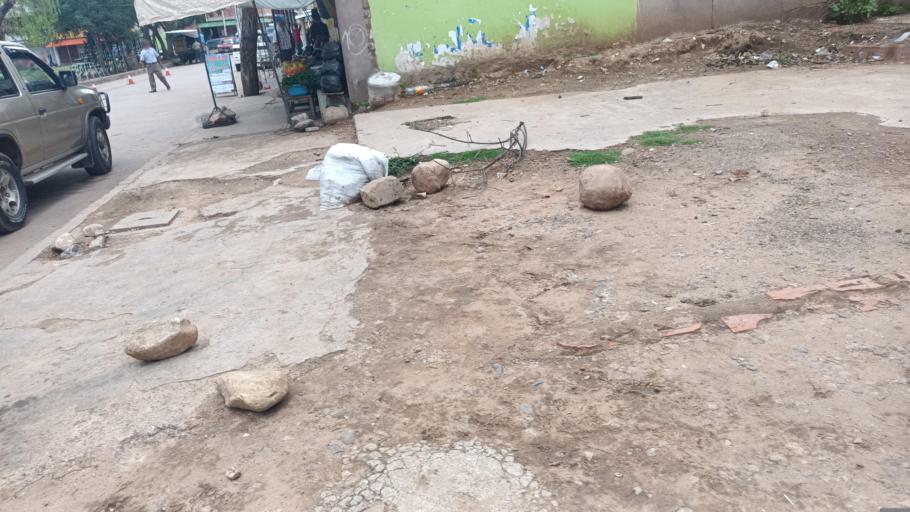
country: BO
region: Tarija
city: Entre Rios
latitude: -21.5285
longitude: -64.1721
